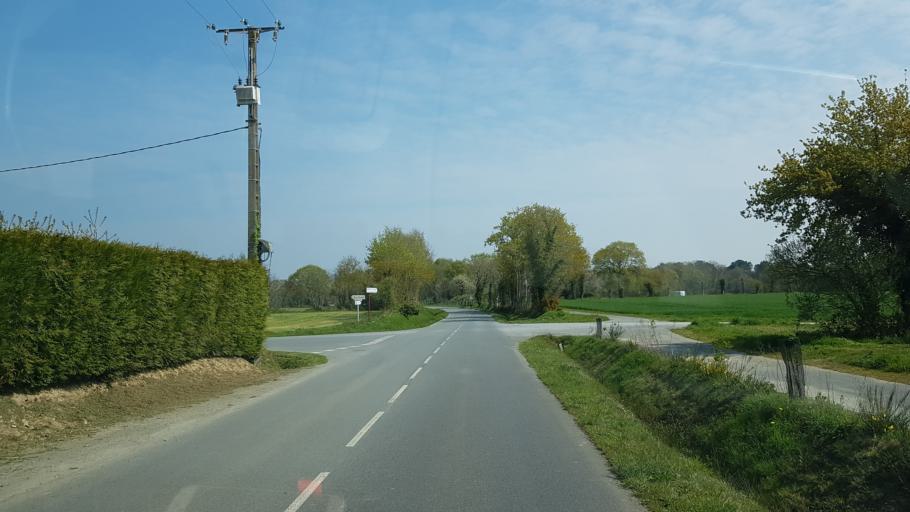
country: FR
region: Brittany
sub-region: Departement du Morbihan
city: Peaule
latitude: 47.5886
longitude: -2.4048
